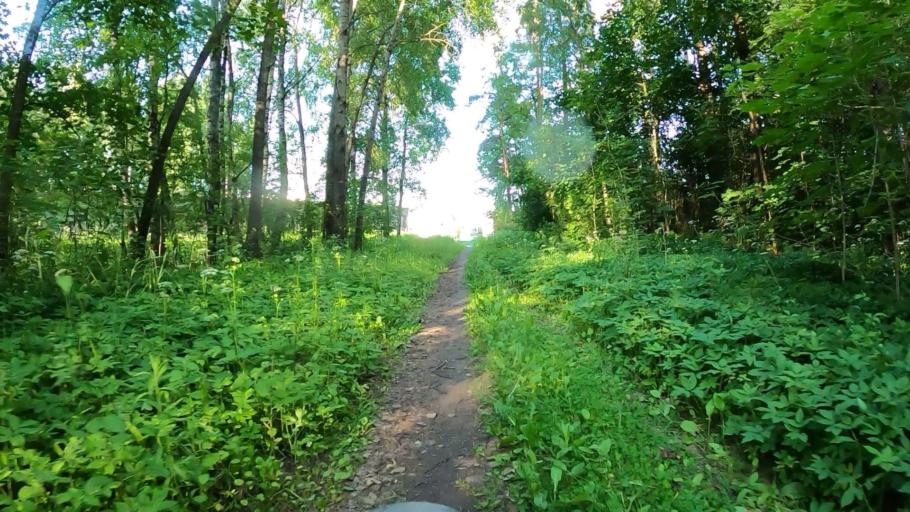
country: LV
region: Stopini
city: Ulbroka
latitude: 56.9301
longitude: 24.2350
